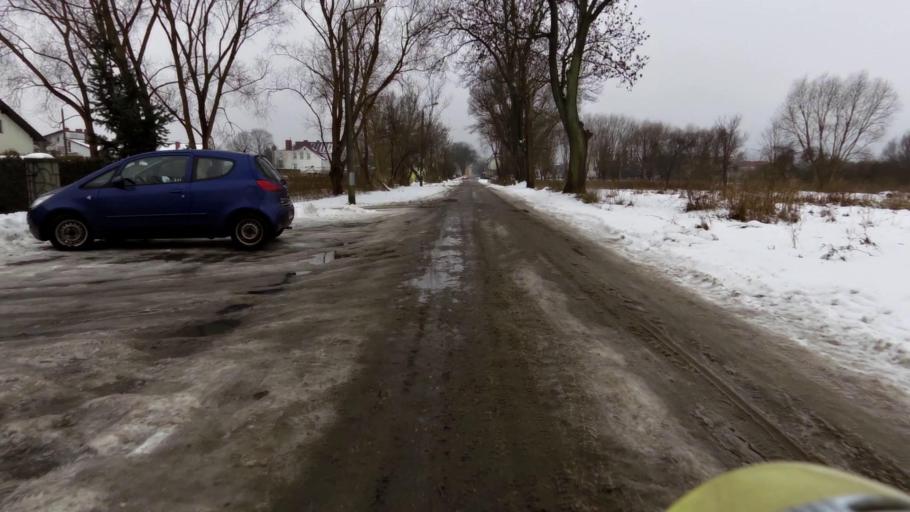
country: PL
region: West Pomeranian Voivodeship
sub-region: Powiat szczecinecki
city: Szczecinek
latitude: 53.7176
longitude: 16.6971
